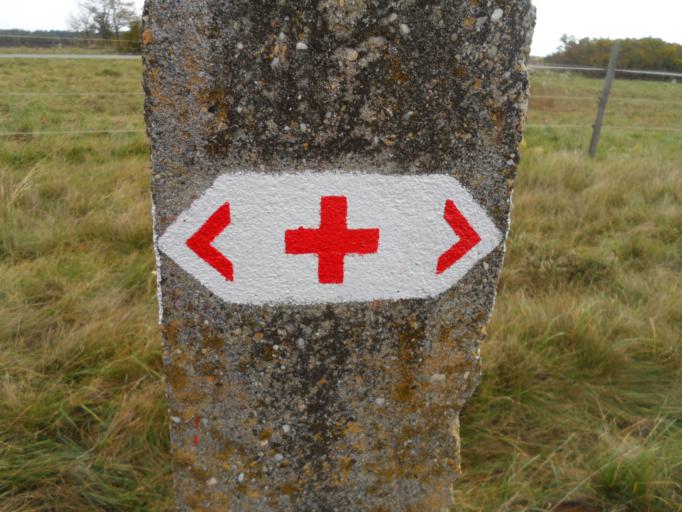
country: HU
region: Veszprem
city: Nemesvamos
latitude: 47.0910
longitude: 17.8686
